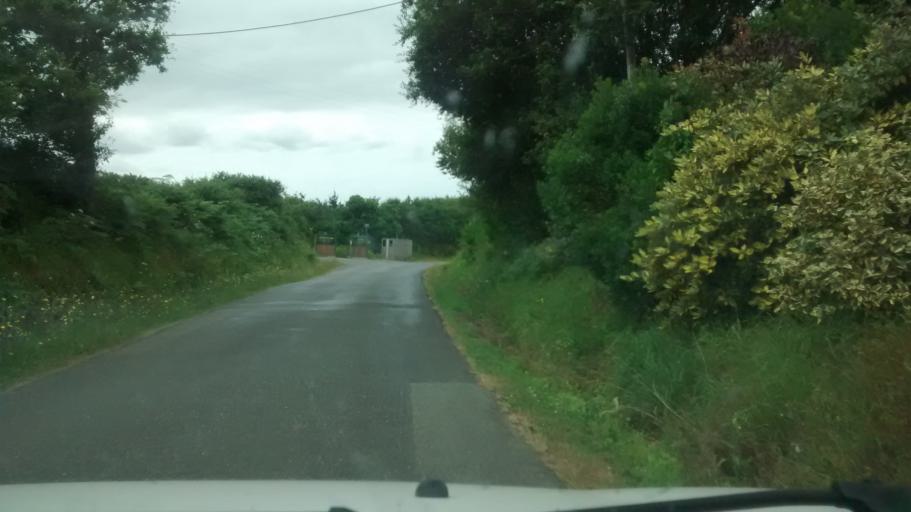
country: FR
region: Brittany
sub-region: Departement du Finistere
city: Lanveoc
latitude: 48.3329
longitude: -4.4377
